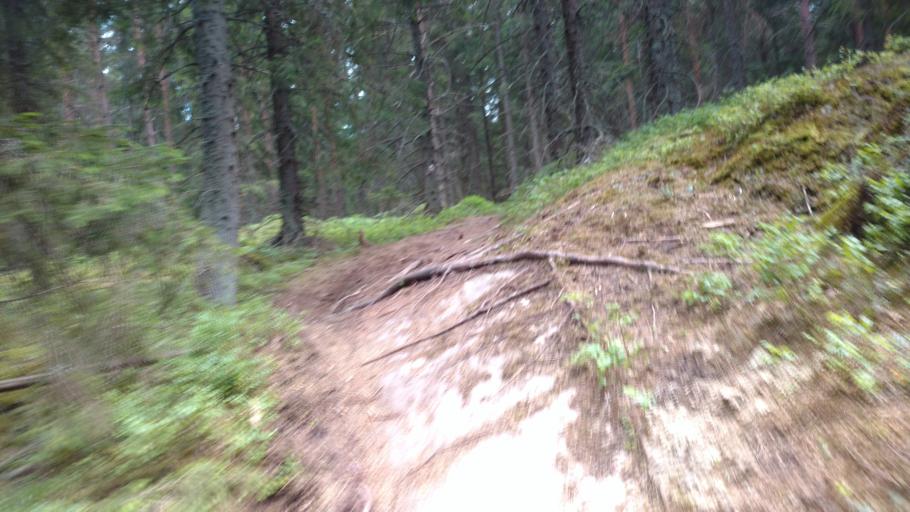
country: FI
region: Uusimaa
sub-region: Raaseporin
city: Pohja
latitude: 60.1181
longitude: 23.5622
